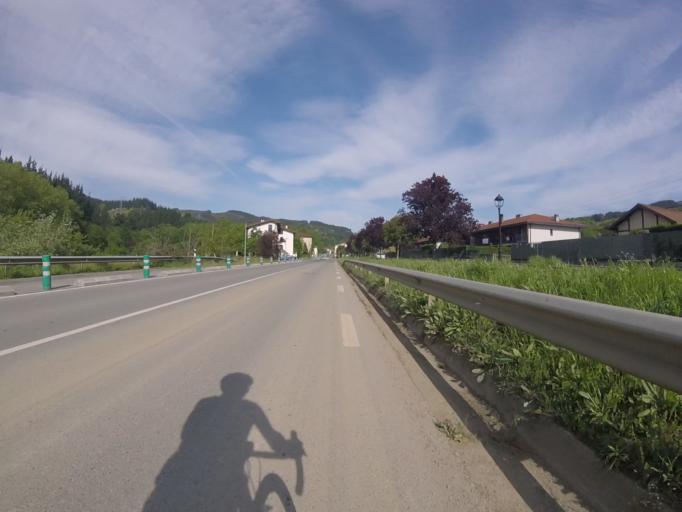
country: ES
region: Basque Country
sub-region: Provincia de Guipuzcoa
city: Gabiria
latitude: 43.0672
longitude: -2.2805
